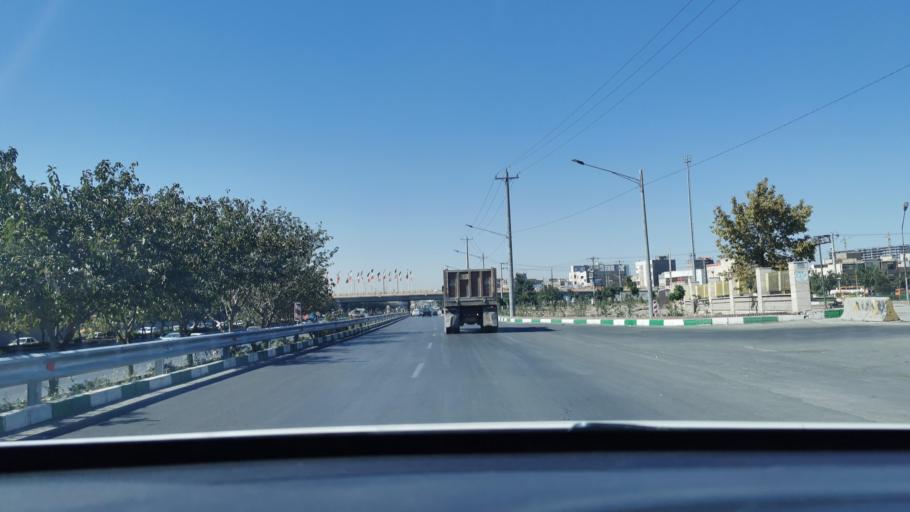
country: IR
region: Razavi Khorasan
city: Mashhad
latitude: 36.3357
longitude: 59.6082
